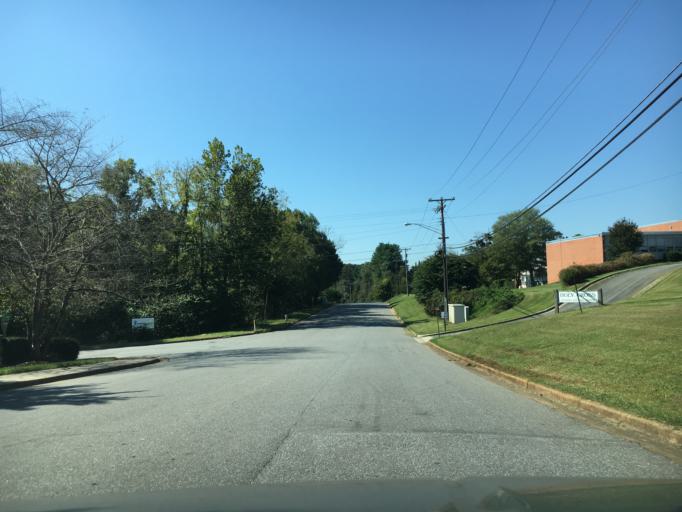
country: US
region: Virginia
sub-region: City of Lynchburg
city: West Lynchburg
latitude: 37.4130
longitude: -79.1764
